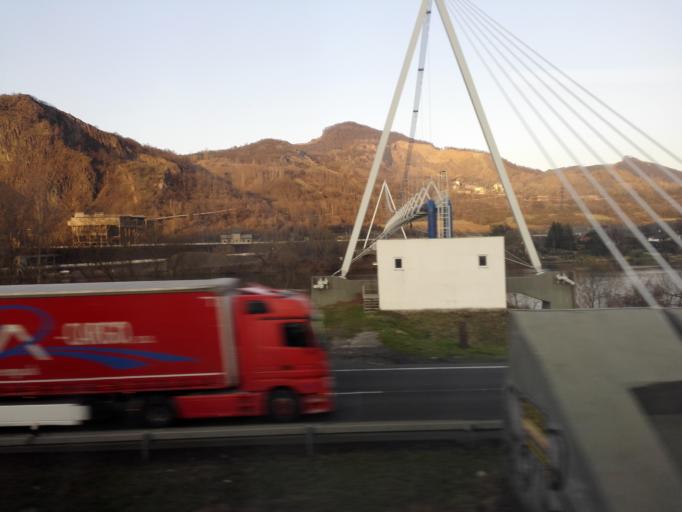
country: CZ
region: Ustecky
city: Lovosice
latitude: 50.5794
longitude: 14.0341
